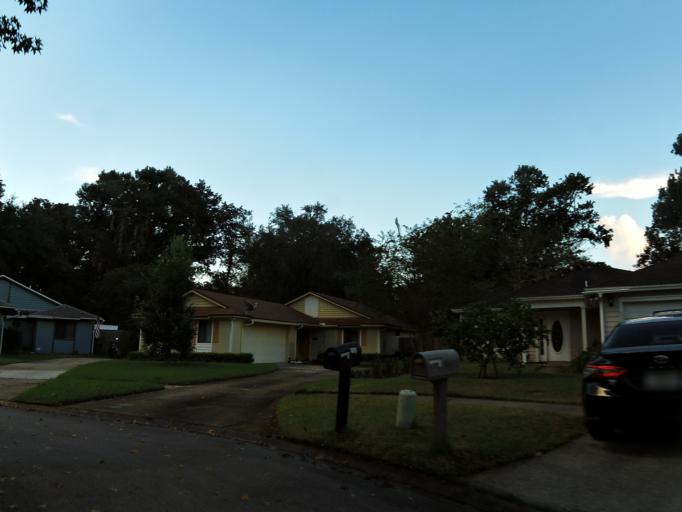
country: US
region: Florida
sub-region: Duval County
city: Jacksonville
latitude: 30.2288
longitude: -81.6022
